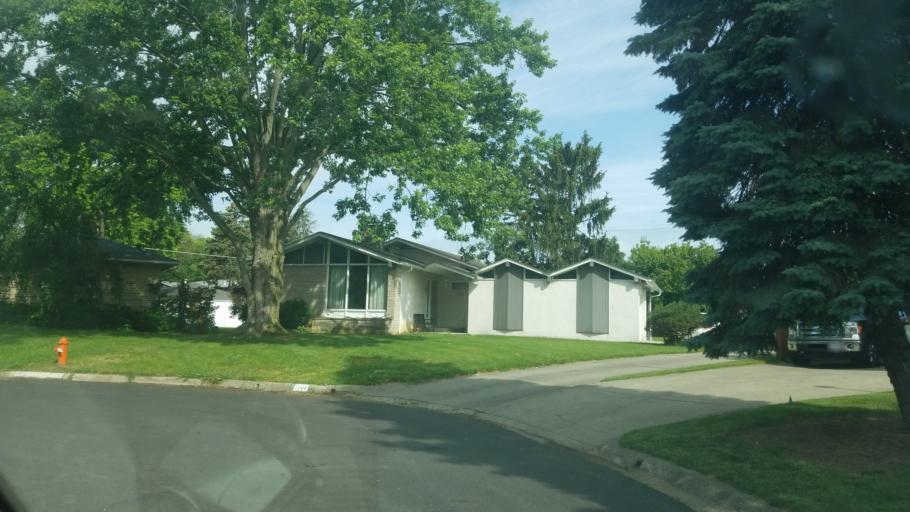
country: US
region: Ohio
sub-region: Franklin County
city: Worthington
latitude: 40.0580
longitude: -82.9883
